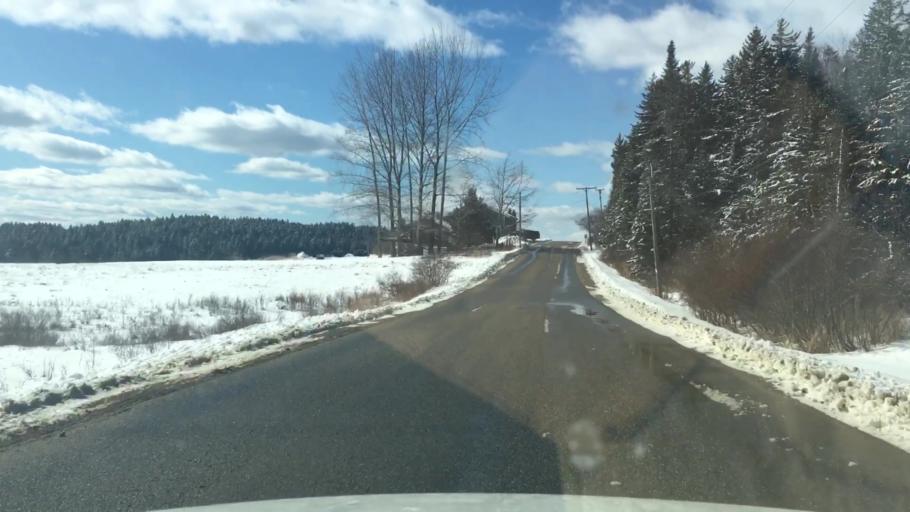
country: US
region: Maine
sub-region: Washington County
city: Machiasport
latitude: 44.6698
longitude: -67.4313
